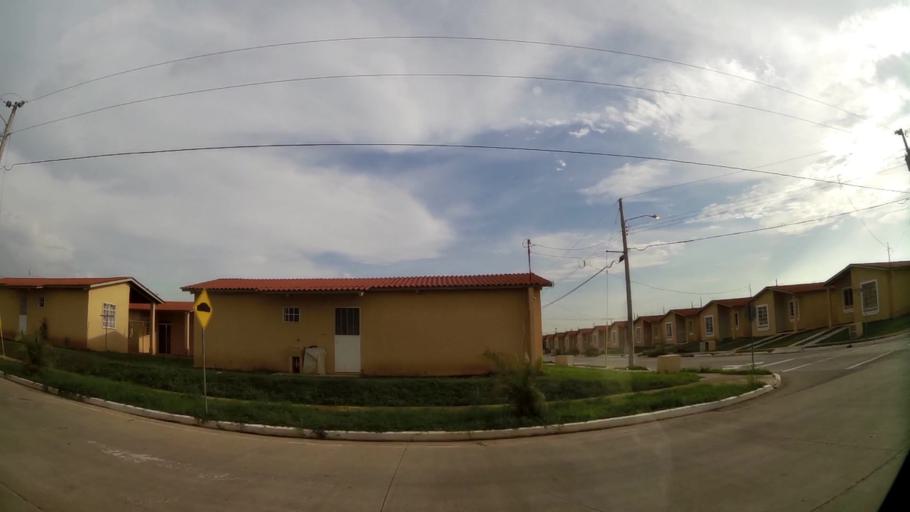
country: PA
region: Panama
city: Tocumen
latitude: 9.0772
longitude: -79.3536
